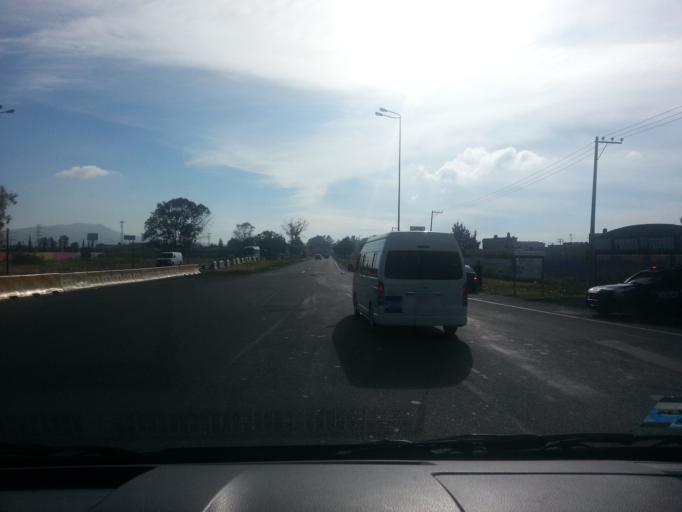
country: MX
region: Mexico
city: Santo Tomas Chiconautla
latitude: 19.6118
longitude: -99.0250
